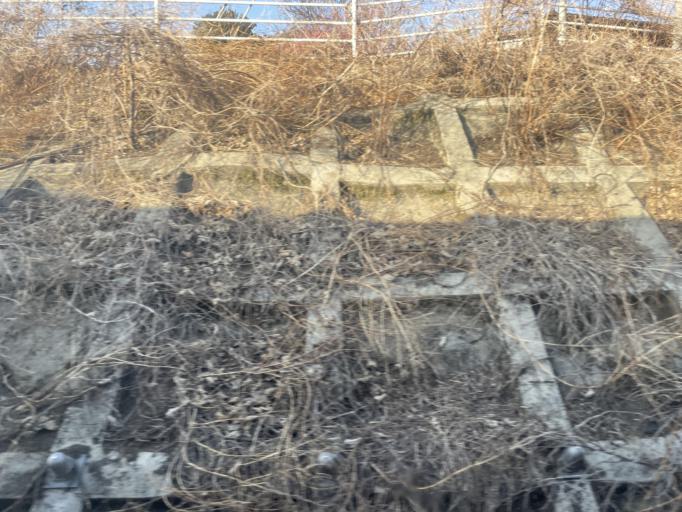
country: JP
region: Gunma
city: Nakanojomachi
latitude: 36.5533
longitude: 138.9134
